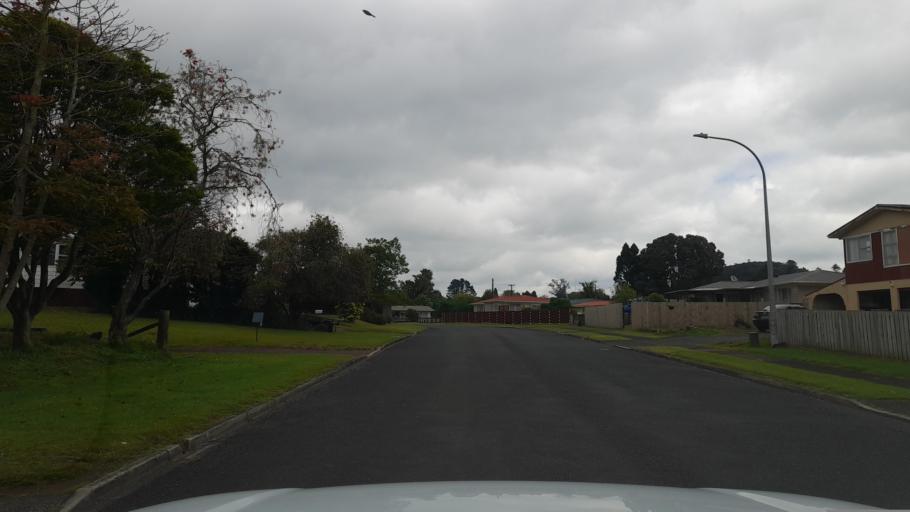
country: NZ
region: Northland
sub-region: Far North District
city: Waimate North
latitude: -35.4020
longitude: 173.7905
